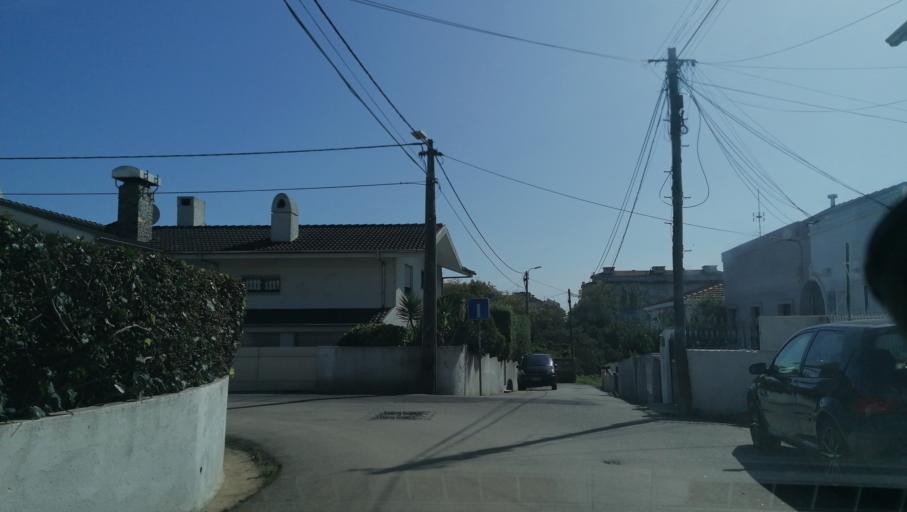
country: PT
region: Aveiro
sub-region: Espinho
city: Espinho
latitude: 41.0142
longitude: -8.6362
